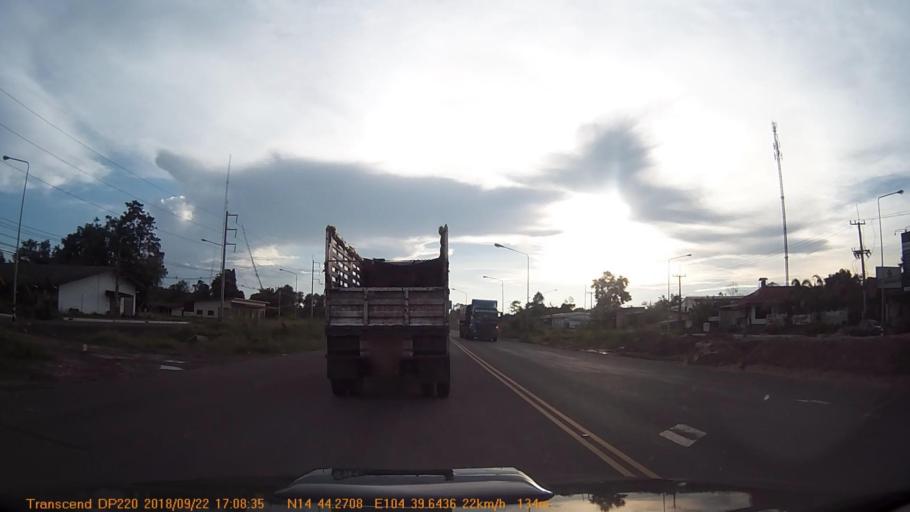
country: TH
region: Sisaket
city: Benchalak
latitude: 14.7379
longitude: 104.6608
